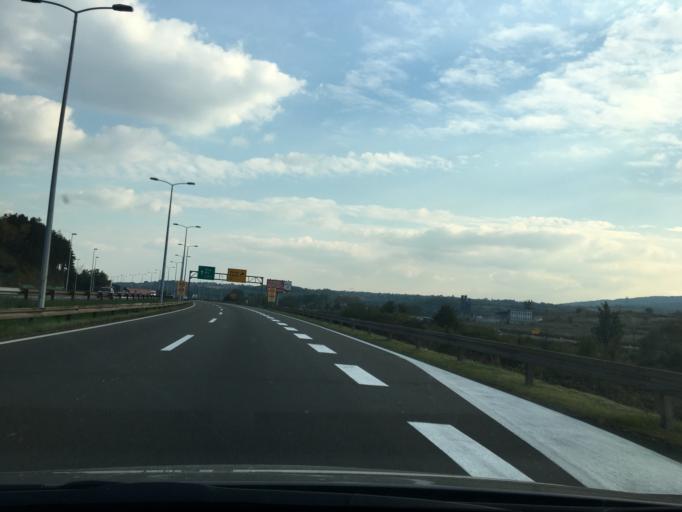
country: RS
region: Central Serbia
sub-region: Belgrade
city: Zvezdara
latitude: 44.7271
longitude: 20.5401
